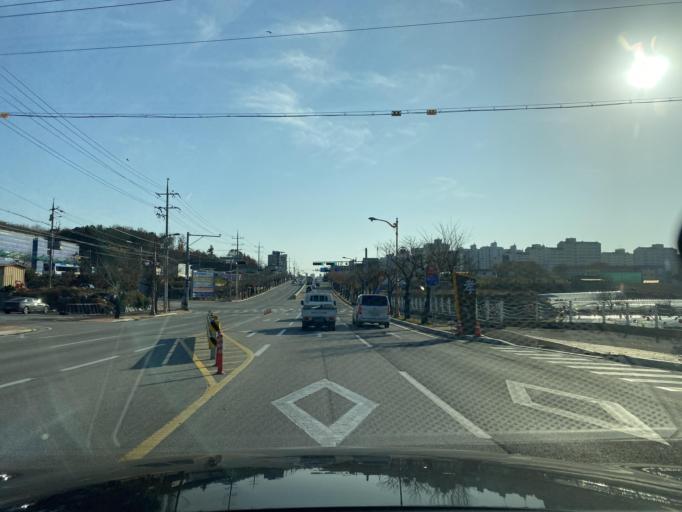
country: KR
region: Chungcheongnam-do
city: Yesan
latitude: 36.7013
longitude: 126.8382
